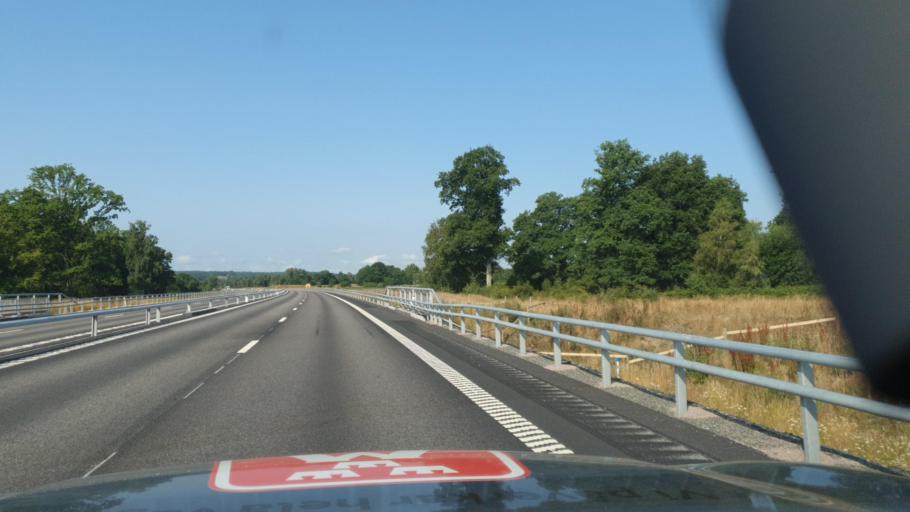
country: SE
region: Skane
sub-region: Kristianstads Kommun
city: Onnestad
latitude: 55.9589
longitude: 13.9373
